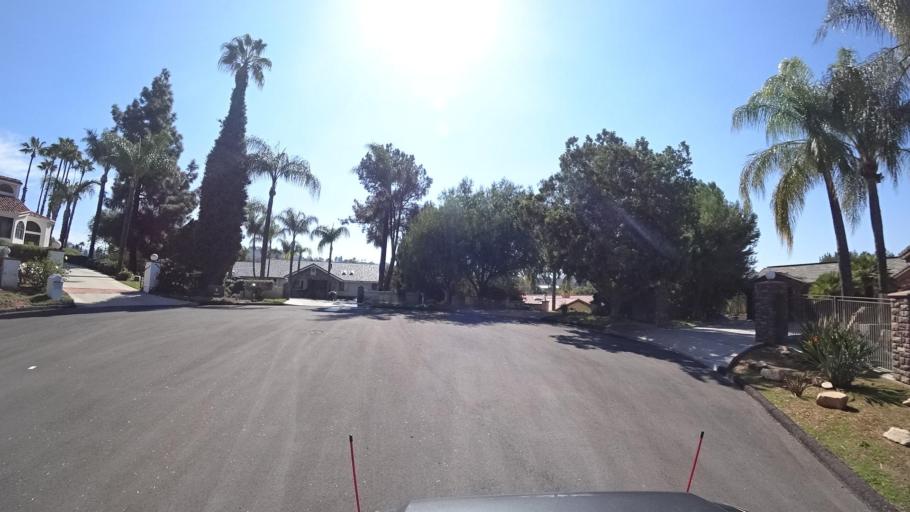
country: US
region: California
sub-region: San Diego County
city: Granite Hills
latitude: 32.7860
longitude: -116.9027
